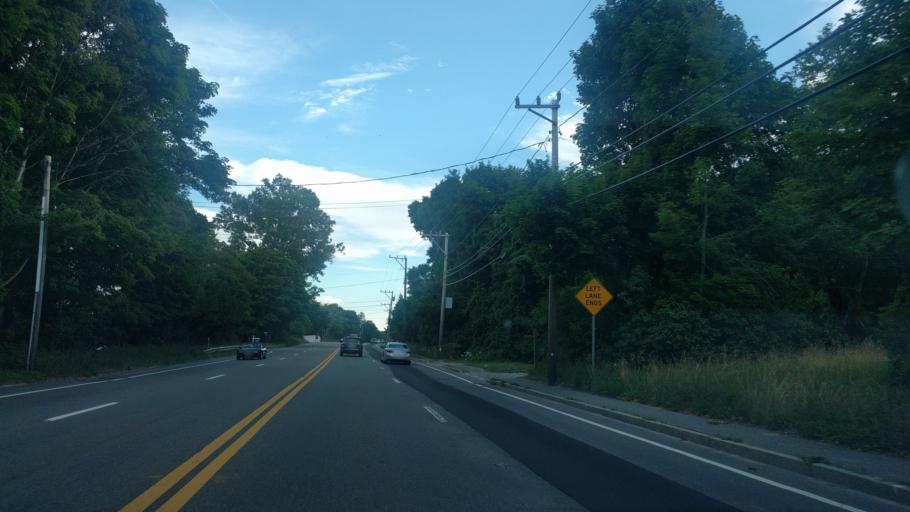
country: US
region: Massachusetts
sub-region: Barnstable County
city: Orleans
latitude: 41.8053
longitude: -69.9761
